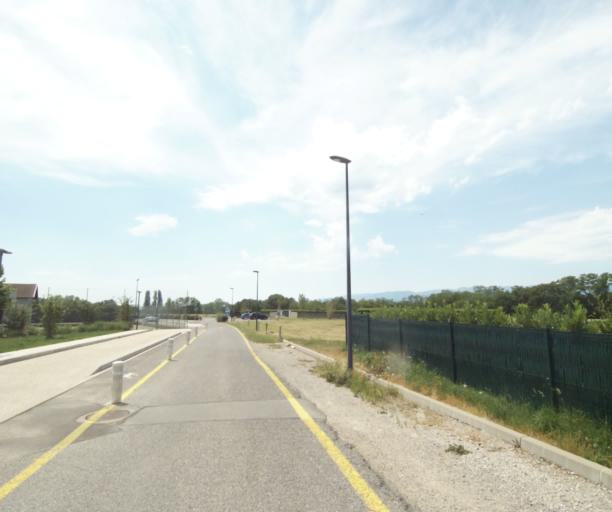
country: FR
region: Rhone-Alpes
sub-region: Departement de la Haute-Savoie
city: Chens-sur-Leman
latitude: 46.3266
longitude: 6.2666
